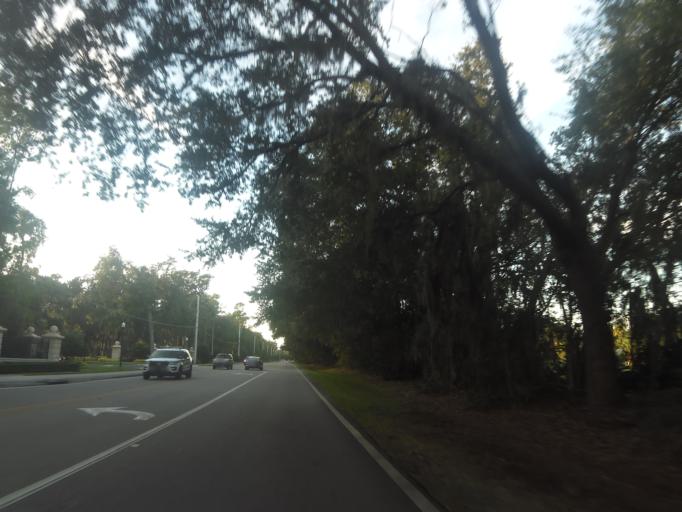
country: US
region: Florida
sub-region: Saint Johns County
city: Palm Valley
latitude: 30.1548
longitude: -81.3807
